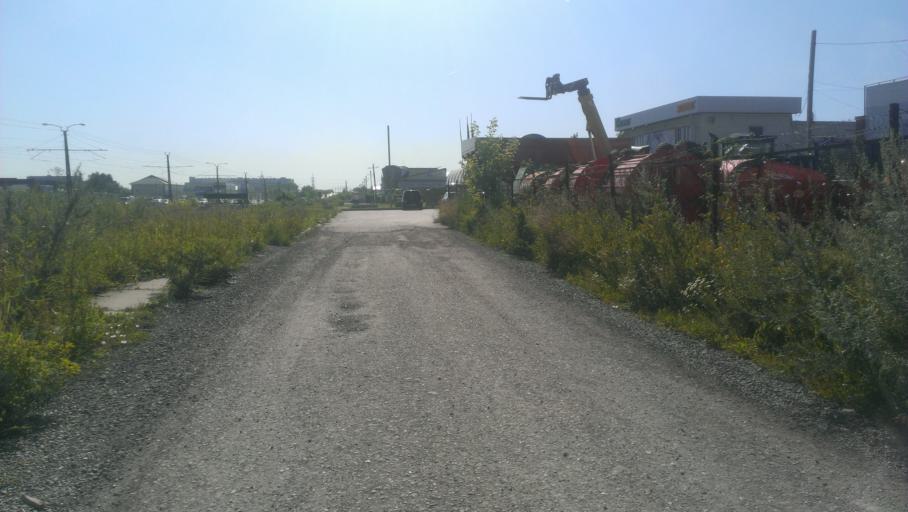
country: RU
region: Altai Krai
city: Novosilikatnyy
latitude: 53.3293
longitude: 83.6609
